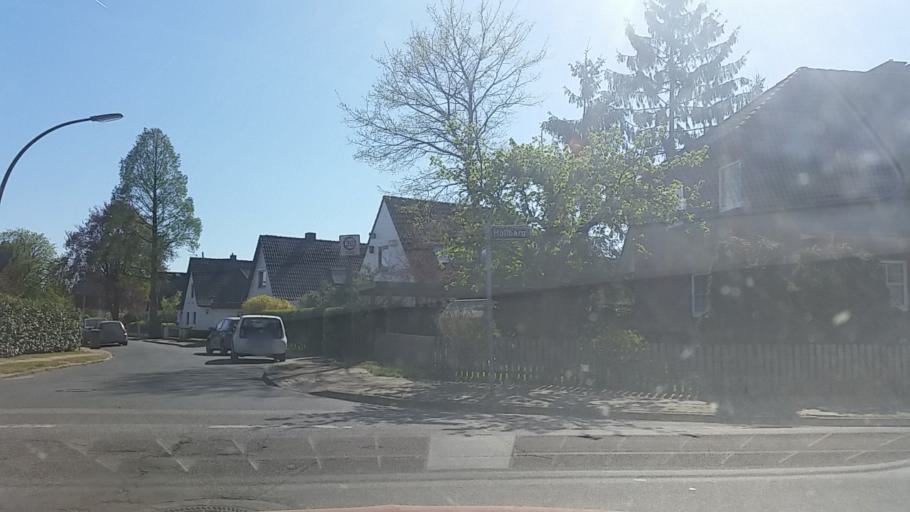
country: DE
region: Schleswig-Holstein
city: Halstenbek
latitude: 53.5836
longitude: 9.8252
